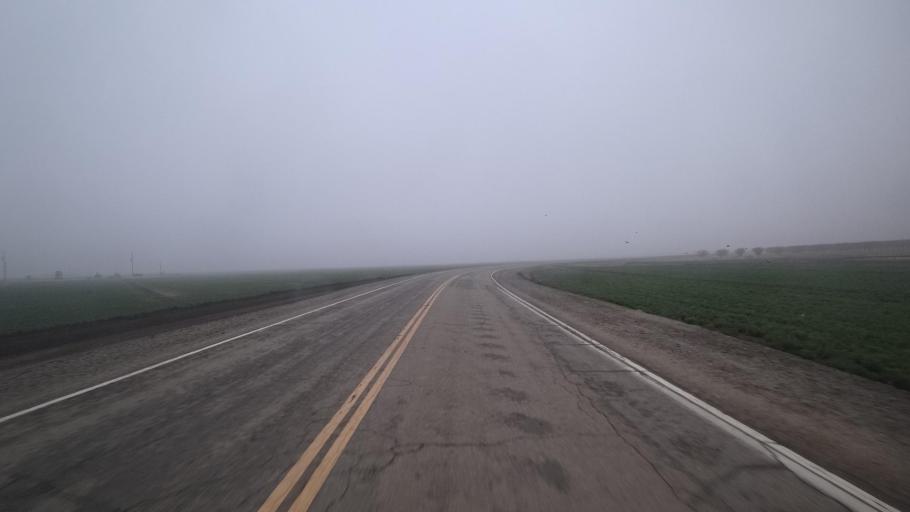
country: US
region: California
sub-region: Kern County
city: Buttonwillow
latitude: 35.4297
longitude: -119.5426
